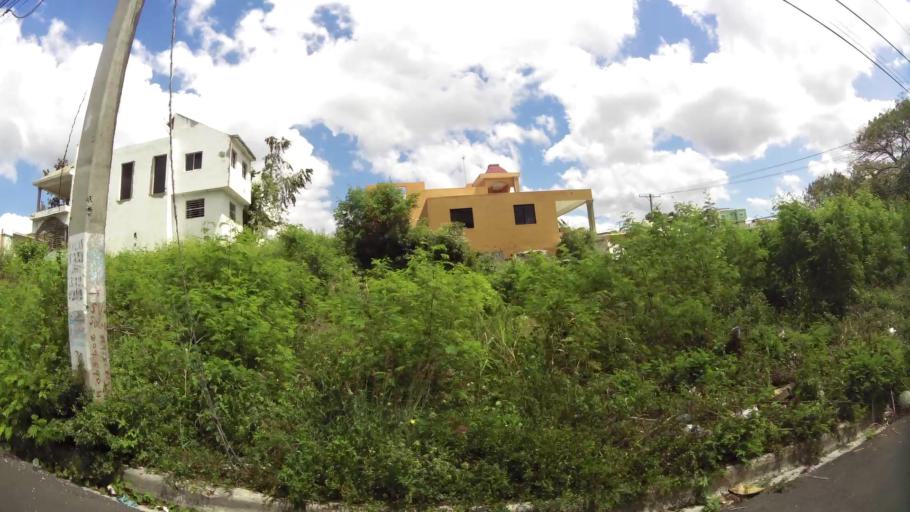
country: DO
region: Nacional
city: La Agustina
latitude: 18.5201
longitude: -69.9195
